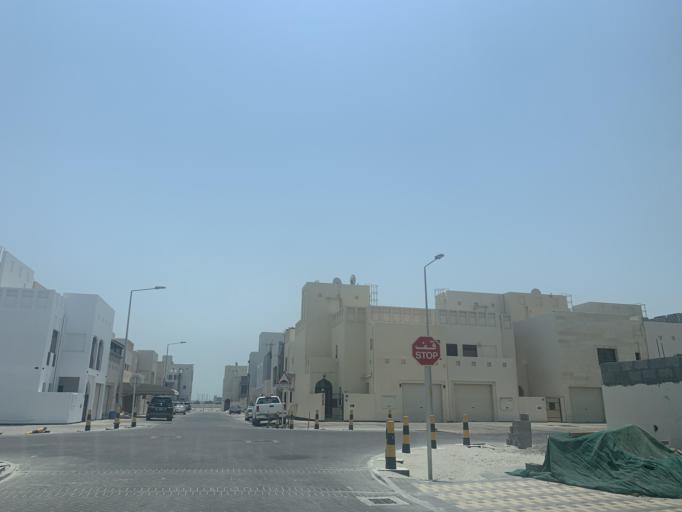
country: BH
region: Muharraq
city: Al Hadd
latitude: 26.2327
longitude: 50.6754
